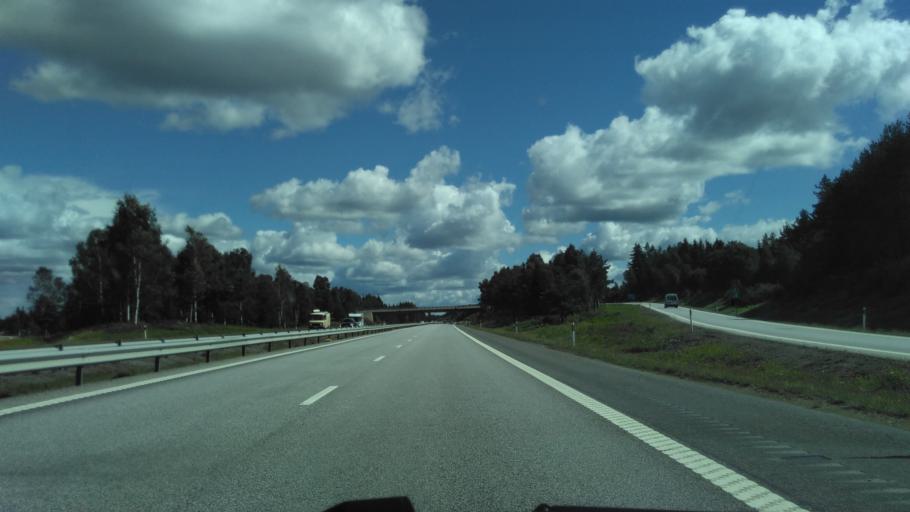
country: SE
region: Vaestra Goetaland
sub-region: Harryda Kommun
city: Hindas
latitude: 57.6756
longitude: 12.3480
